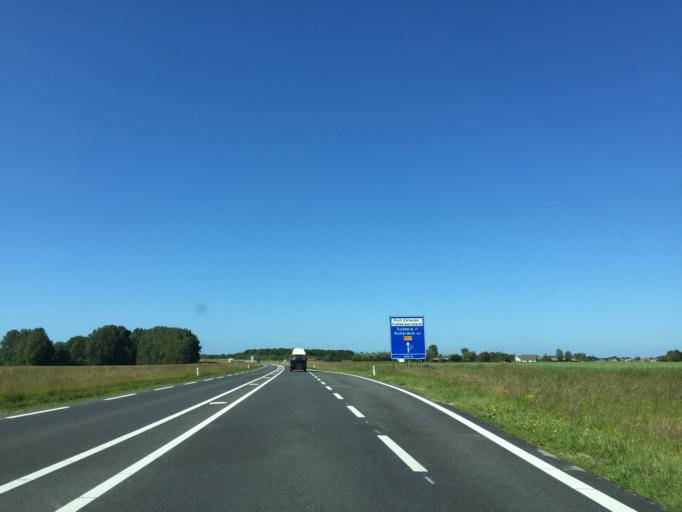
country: NL
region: Zeeland
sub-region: Schouwen-Duiveland
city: Scharendijke
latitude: 51.7255
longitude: 3.8221
